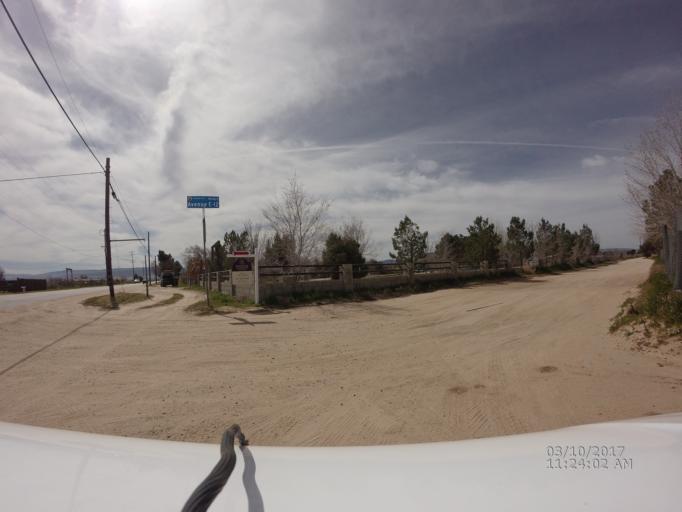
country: US
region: California
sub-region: Los Angeles County
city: Quartz Hill
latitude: 34.7511
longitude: -118.2901
